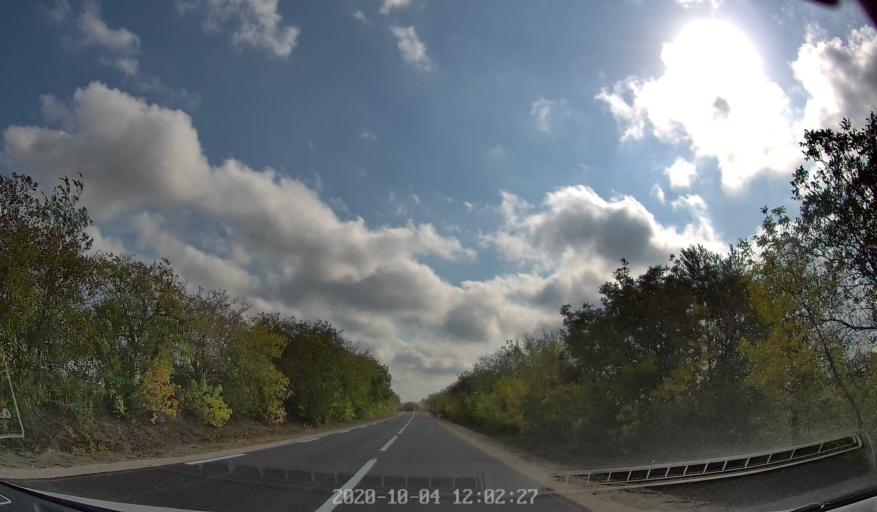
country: MD
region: Rezina
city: Saharna
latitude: 47.6167
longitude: 28.9076
